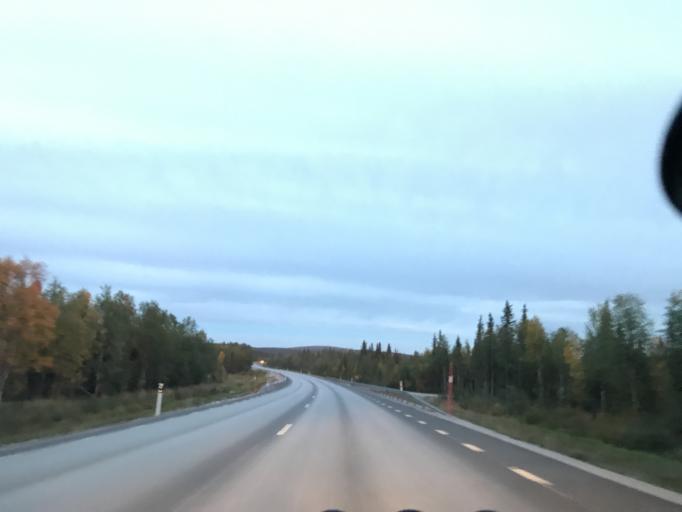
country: SE
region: Norrbotten
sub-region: Gallivare Kommun
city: Malmberget
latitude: 67.6473
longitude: 21.0277
